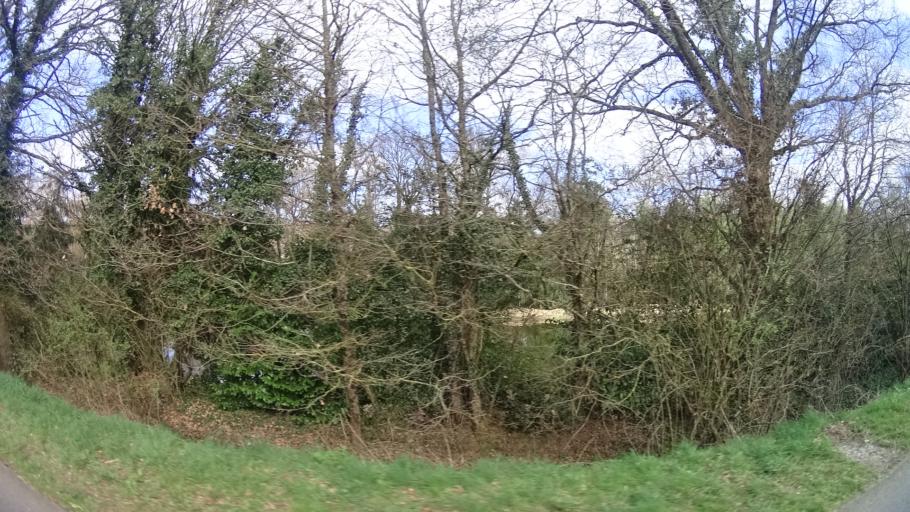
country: FR
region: Brittany
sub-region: Departement du Morbihan
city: Caro
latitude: 47.8430
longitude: -2.3180
